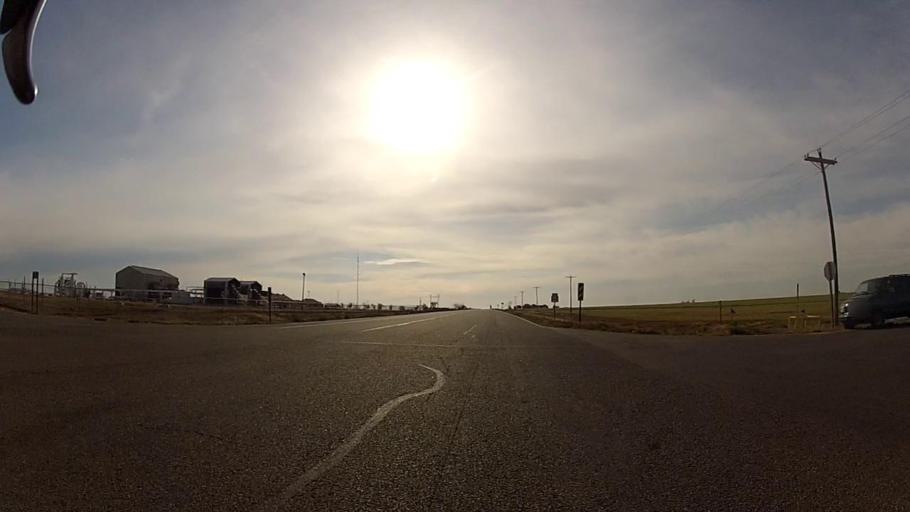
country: US
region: Kansas
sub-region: Grant County
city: Ulysses
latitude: 37.5766
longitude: -101.4901
